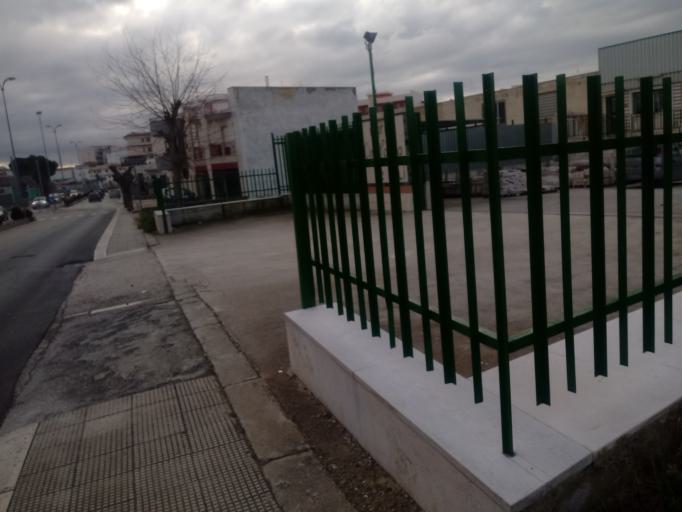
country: IT
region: Apulia
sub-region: Provincia di Barletta - Andria - Trani
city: Andria
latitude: 41.2172
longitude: 16.2979
